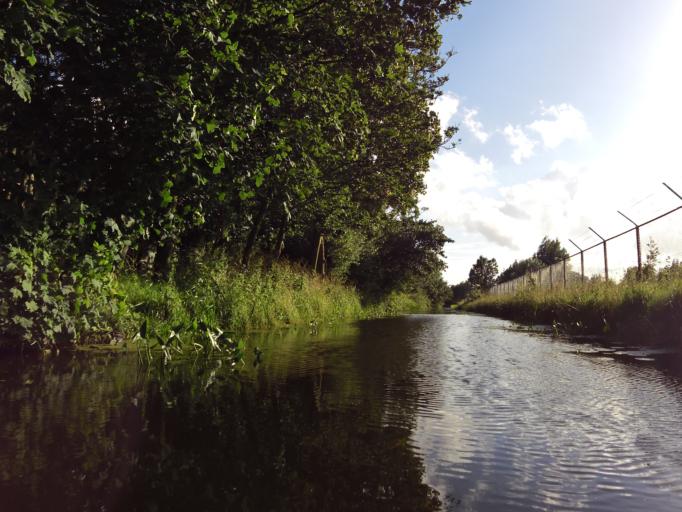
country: NL
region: South Holland
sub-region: Gemeente Wassenaar
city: Wassenaar
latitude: 52.1576
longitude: 4.4021
